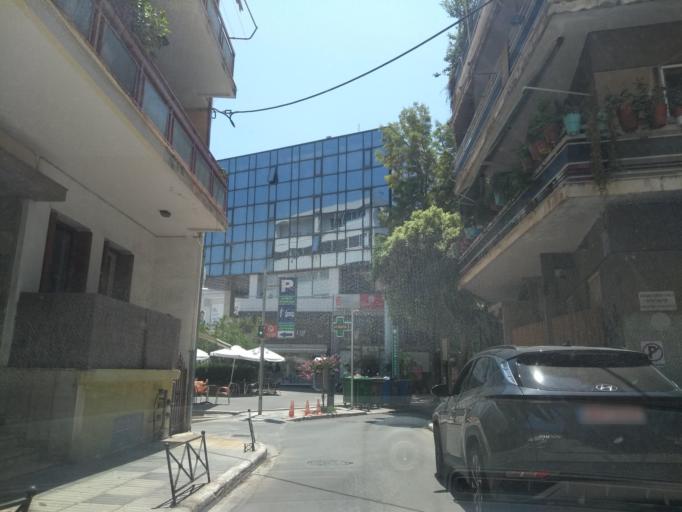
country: GR
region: Crete
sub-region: Nomos Chanias
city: Chania
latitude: 35.5120
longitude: 24.0219
